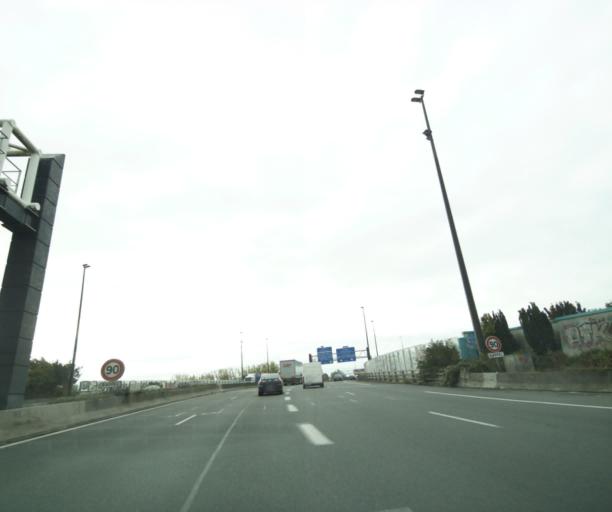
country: FR
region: Nord-Pas-de-Calais
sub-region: Departement du Nord
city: La Madeleine
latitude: 50.6244
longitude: 3.0845
